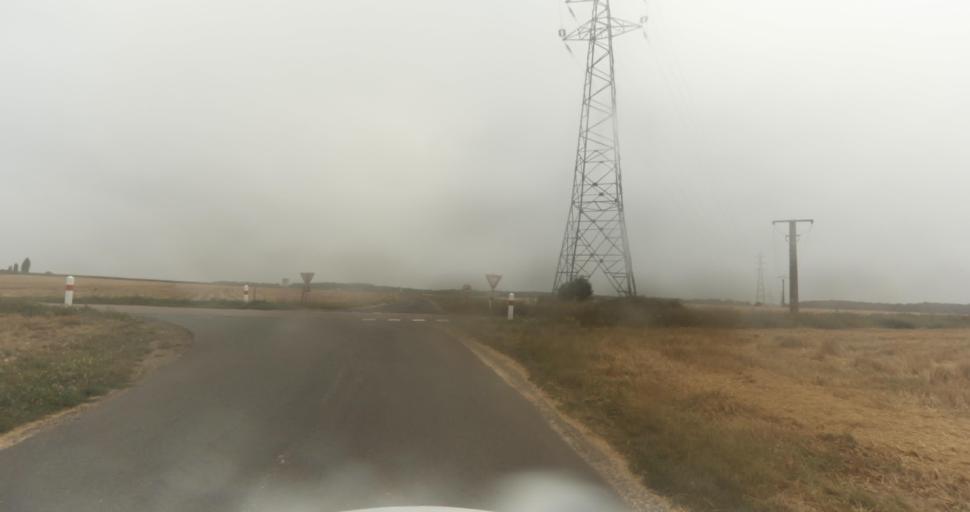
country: FR
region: Centre
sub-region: Departement d'Eure-et-Loir
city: Saint-Lubin-des-Joncherets
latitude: 48.7775
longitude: 1.2145
